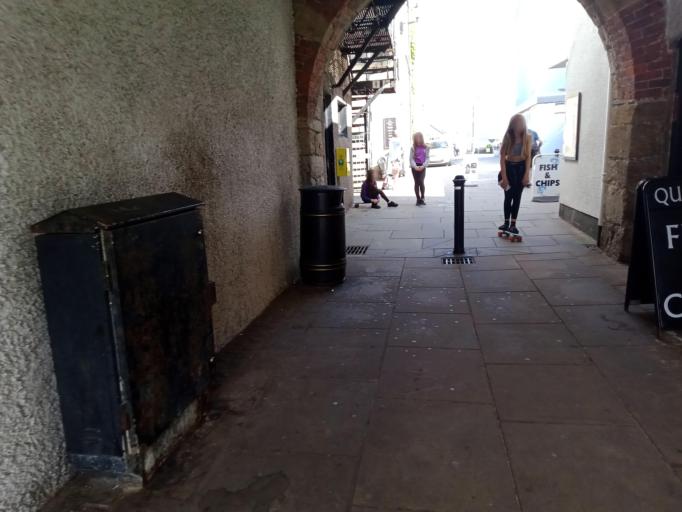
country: GB
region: Wales
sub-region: Anglesey
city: Beaumaris
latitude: 53.2631
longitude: -4.0923
